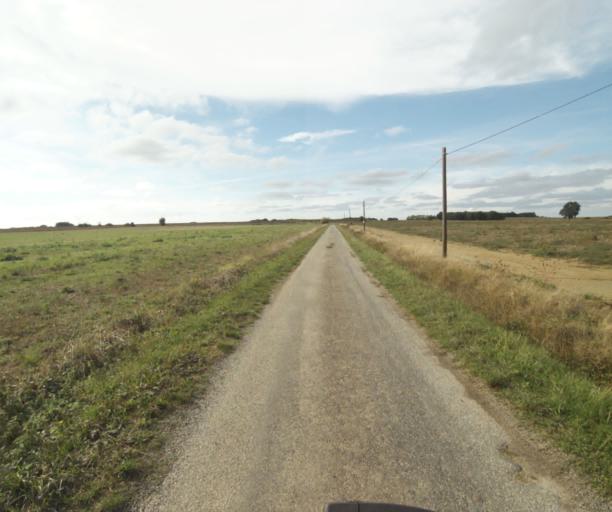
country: FR
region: Midi-Pyrenees
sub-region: Departement du Tarn-et-Garonne
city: Saint-Porquier
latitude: 43.9466
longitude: 1.1307
